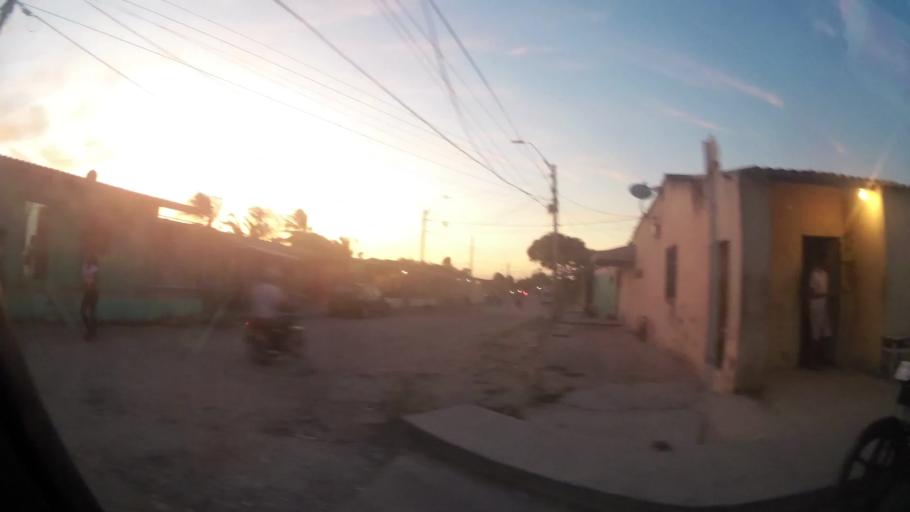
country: CO
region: Atlantico
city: Barranquilla
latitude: 10.9493
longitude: -74.8266
